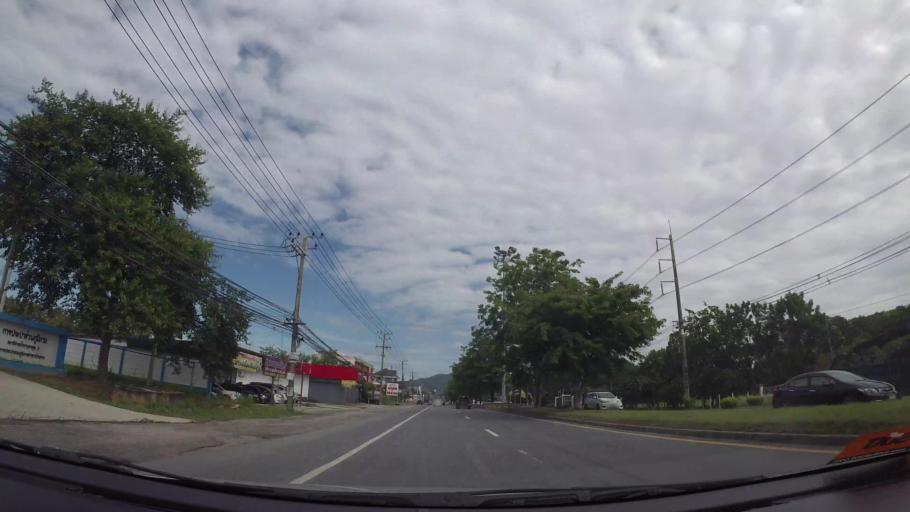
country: TH
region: Rayong
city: Ban Chang
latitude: 12.7321
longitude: 101.1362
